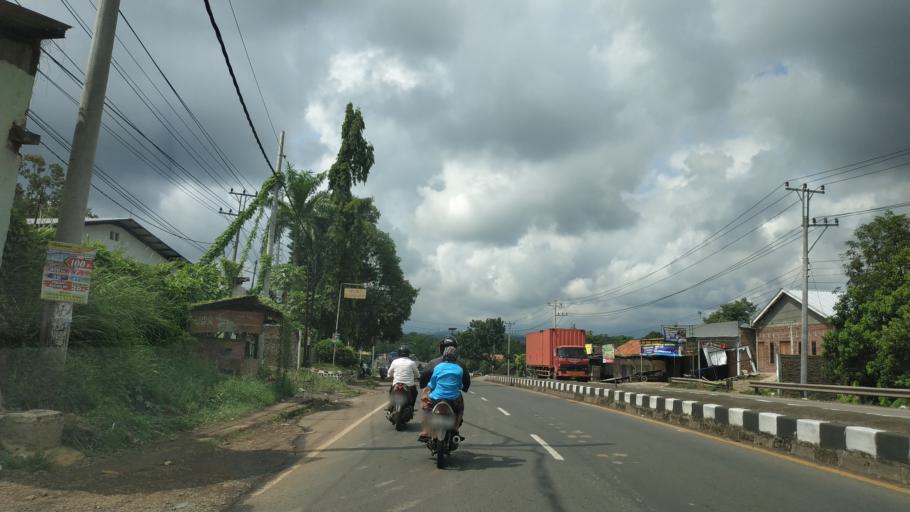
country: ID
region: Central Java
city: Pekalongan
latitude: -6.9440
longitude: 109.7766
